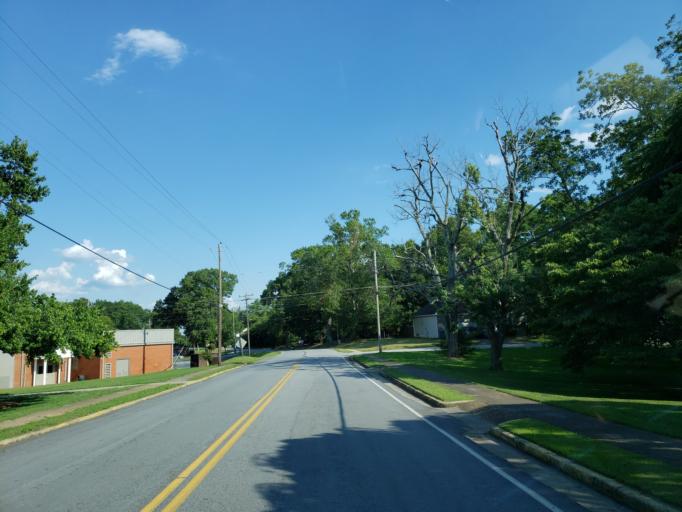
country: US
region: Georgia
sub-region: Haralson County
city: Bremen
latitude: 33.7177
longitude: -85.1399
